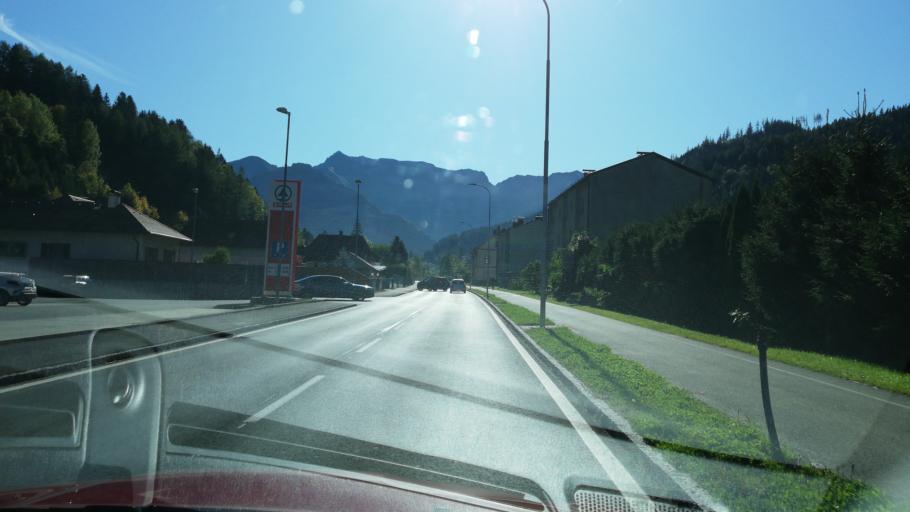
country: AT
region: Styria
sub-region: Politischer Bezirk Leoben
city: Eisenerz
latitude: 47.5552
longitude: 14.8713
